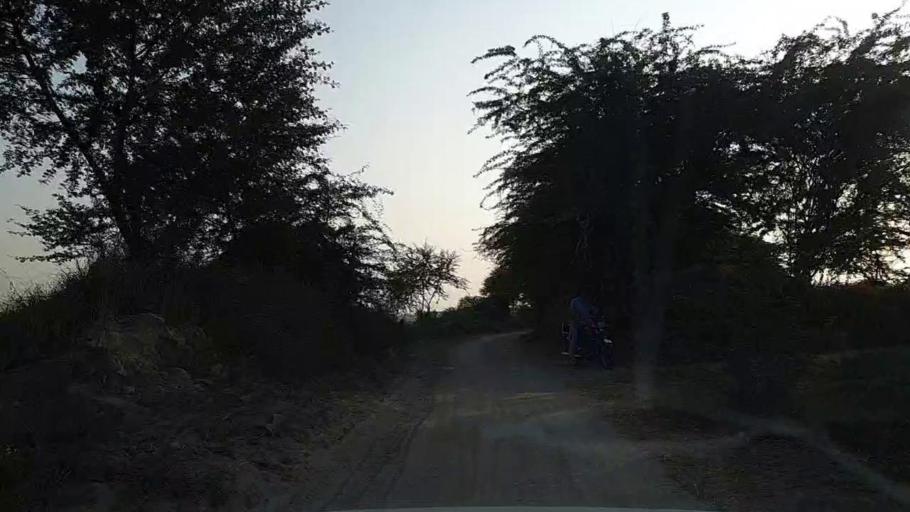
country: PK
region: Sindh
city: Daro Mehar
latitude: 24.7586
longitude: 68.1908
